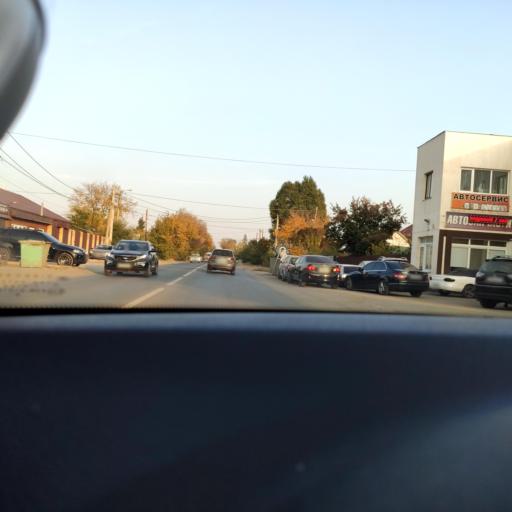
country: RU
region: Samara
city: Petra-Dubrava
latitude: 53.2525
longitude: 50.3323
